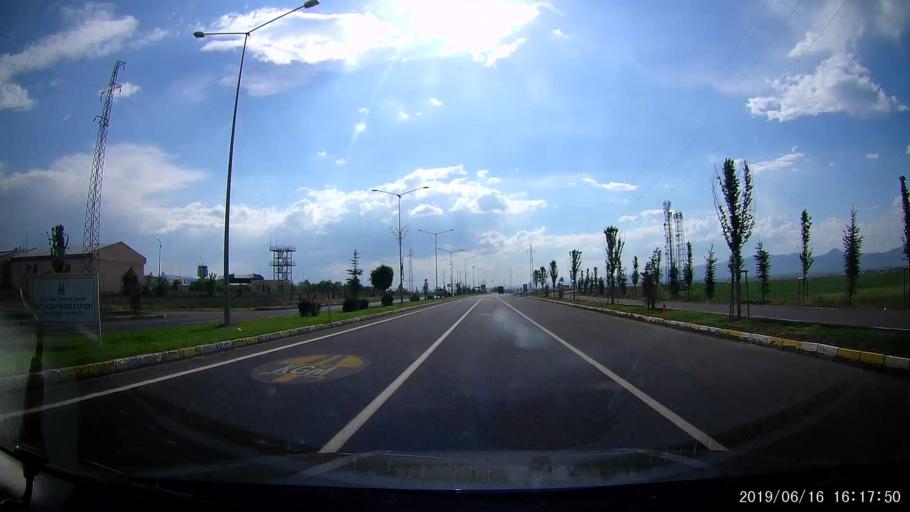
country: TR
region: Erzurum
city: Ilica
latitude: 39.9643
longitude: 41.1799
